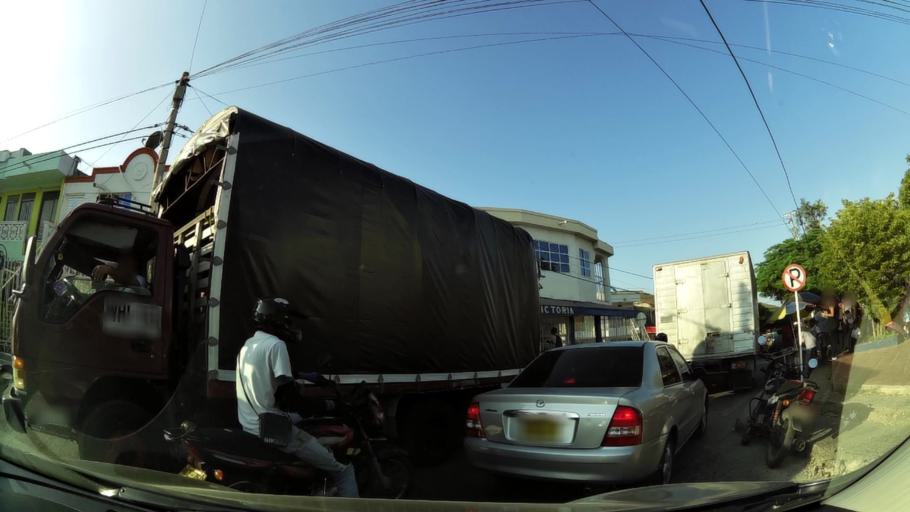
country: CO
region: Bolivar
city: Cartagena
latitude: 10.3797
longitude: -75.4823
